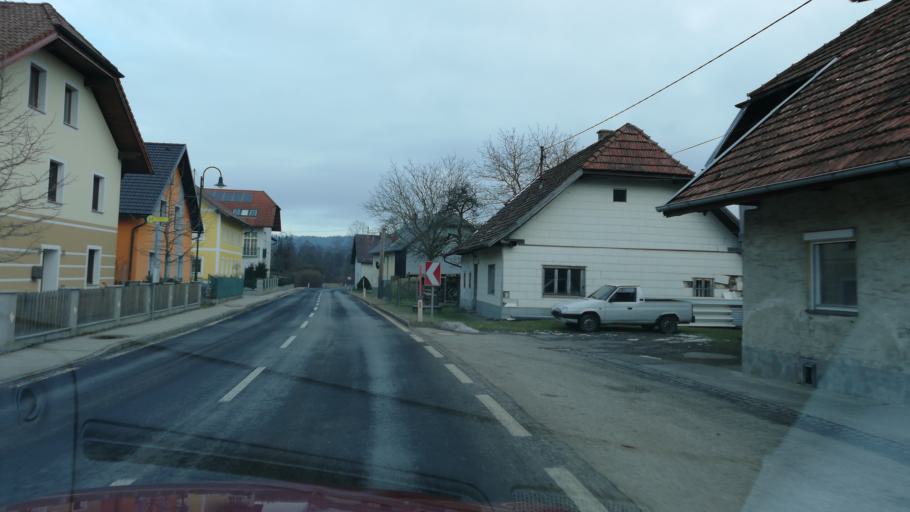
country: AT
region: Upper Austria
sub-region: Politischer Bezirk Vocklabruck
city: Niederthalheim
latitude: 48.1855
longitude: 13.7328
